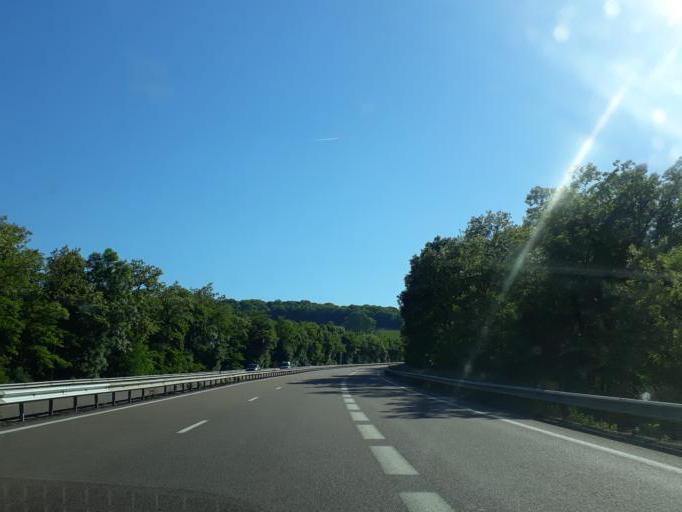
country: FR
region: Bourgogne
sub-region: Departement de la Cote-d'Or
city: Fleurey-sur-Ouche
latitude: 47.2905
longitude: 4.7107
